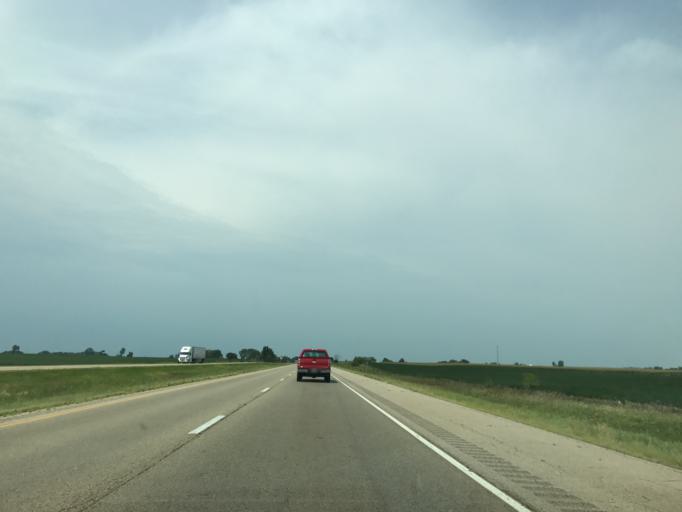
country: US
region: Illinois
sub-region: Bureau County
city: Ladd
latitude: 41.3904
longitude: -89.2849
